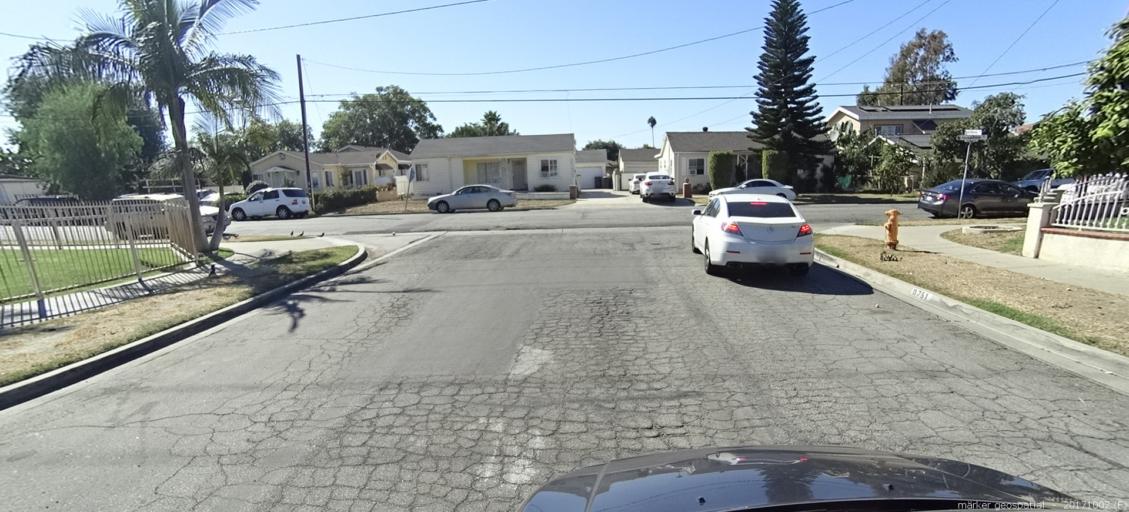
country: US
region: California
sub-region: Orange County
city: Stanton
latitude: 33.7753
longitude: -117.9793
